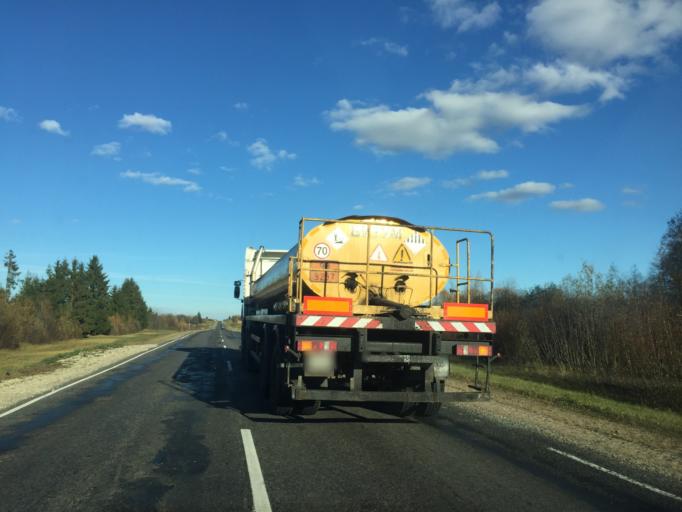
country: BY
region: Vitebsk
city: Dzisna
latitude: 55.2781
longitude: 28.1631
